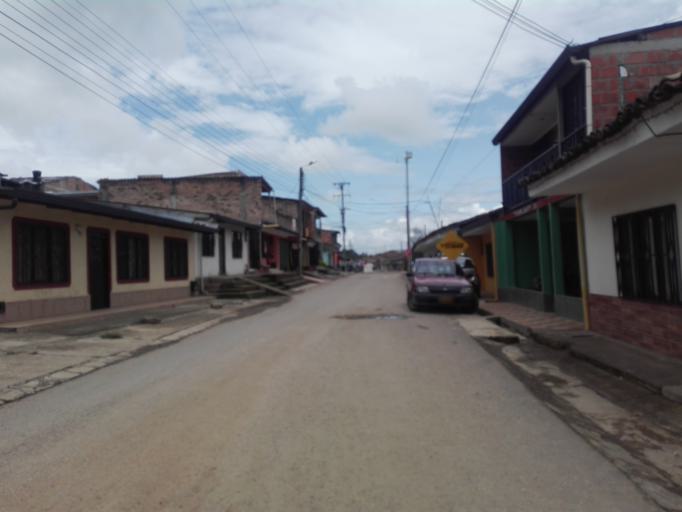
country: CO
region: Cauca
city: Popayan
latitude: 2.3511
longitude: -76.6738
